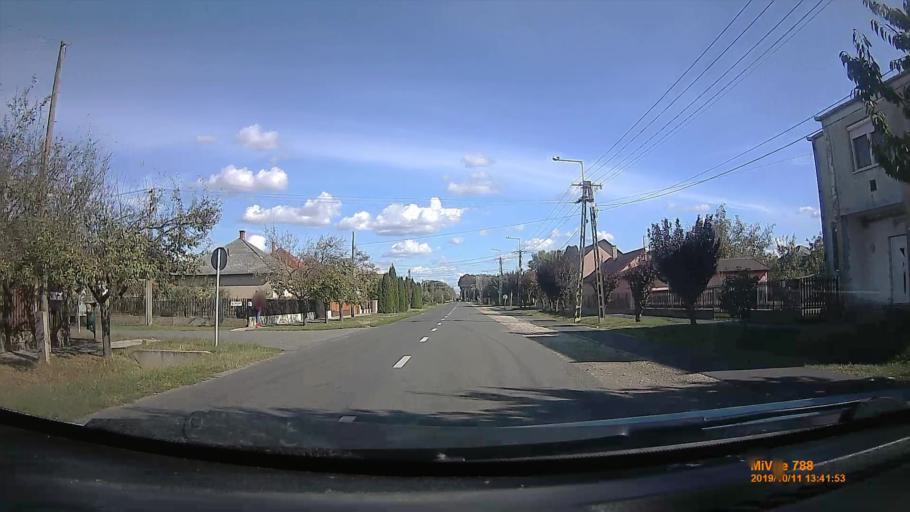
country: HU
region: Hajdu-Bihar
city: Balmazujvaros
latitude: 47.5395
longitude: 21.3392
